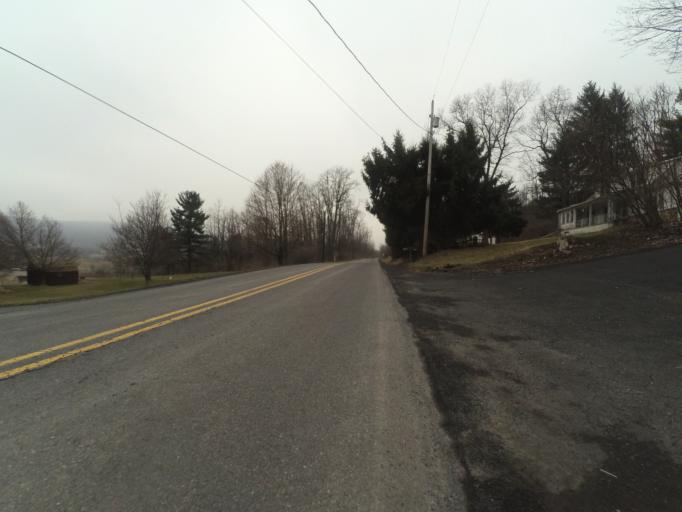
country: US
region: Pennsylvania
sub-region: Centre County
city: Centre Hall
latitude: 40.8304
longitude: -77.5922
